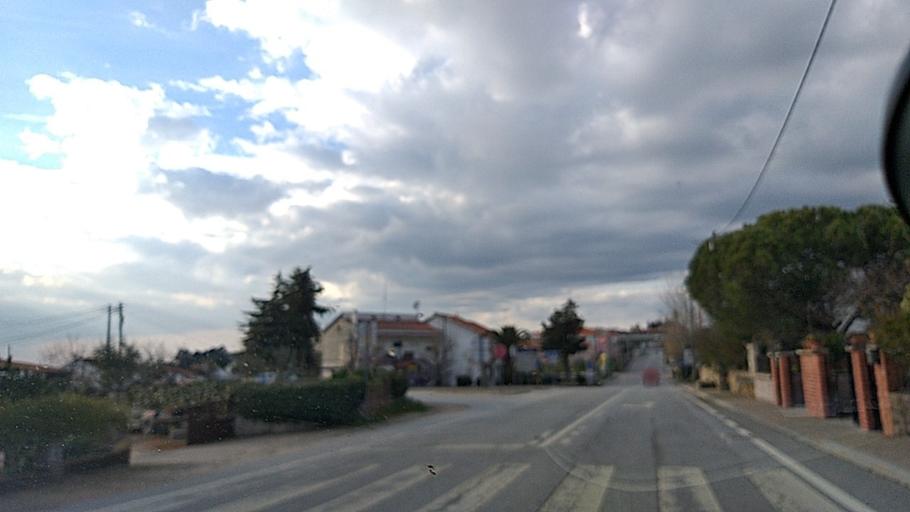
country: ES
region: Castille and Leon
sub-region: Provincia de Salamanca
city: Aldea del Obispo
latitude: 40.7199
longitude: -6.9019
